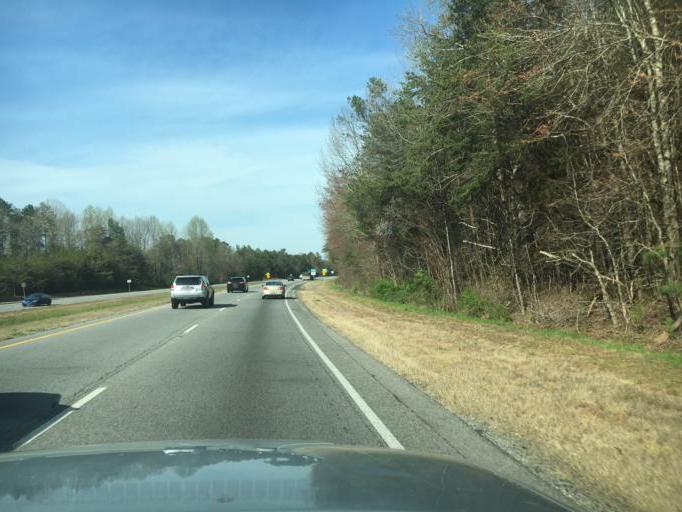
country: US
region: Georgia
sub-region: Habersham County
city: Raoul
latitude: 34.4435
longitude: -83.6255
